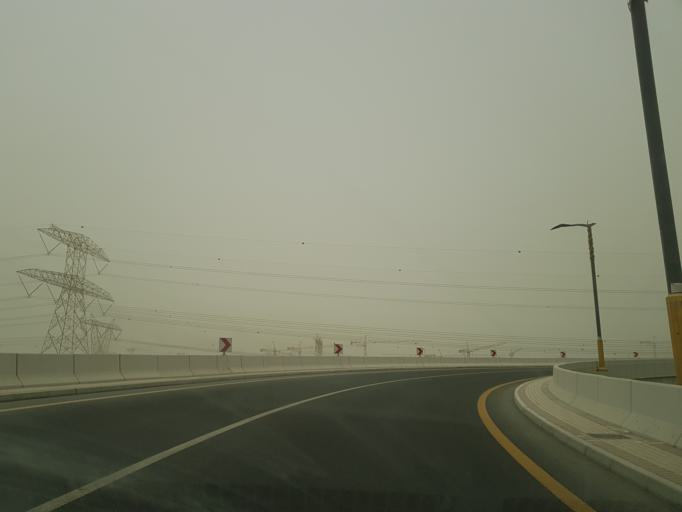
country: AE
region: Dubai
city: Dubai
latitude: 25.1673
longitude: 55.3022
